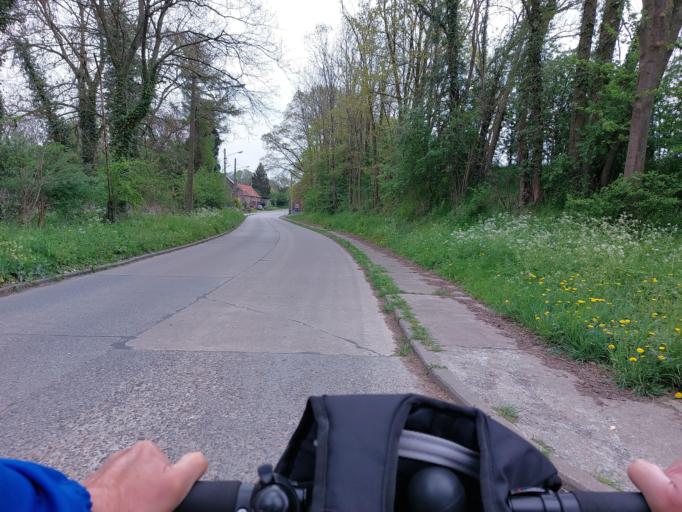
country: BE
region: Wallonia
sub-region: Province du Hainaut
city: Dour
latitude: 50.3655
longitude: 3.7304
